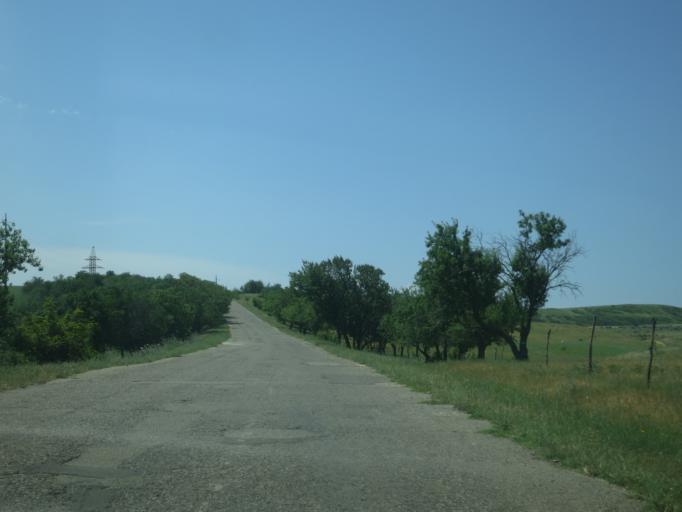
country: GE
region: Kakheti
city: Sagarejo
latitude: 41.6387
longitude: 45.3583
